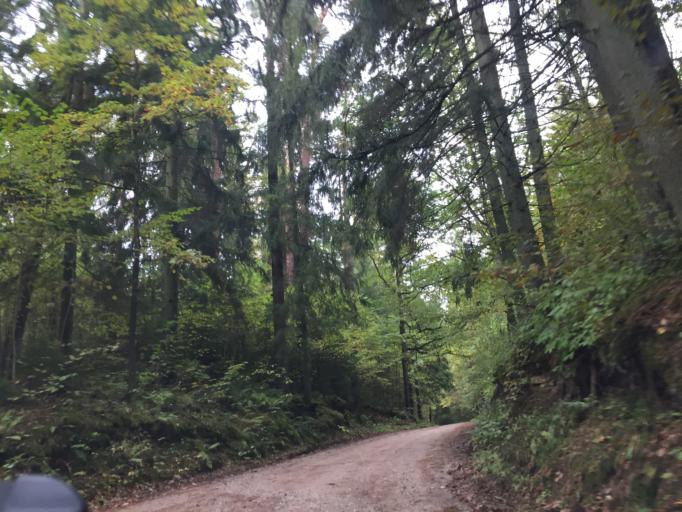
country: LV
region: Auces Novads
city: Auce
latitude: 56.5471
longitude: 23.0178
